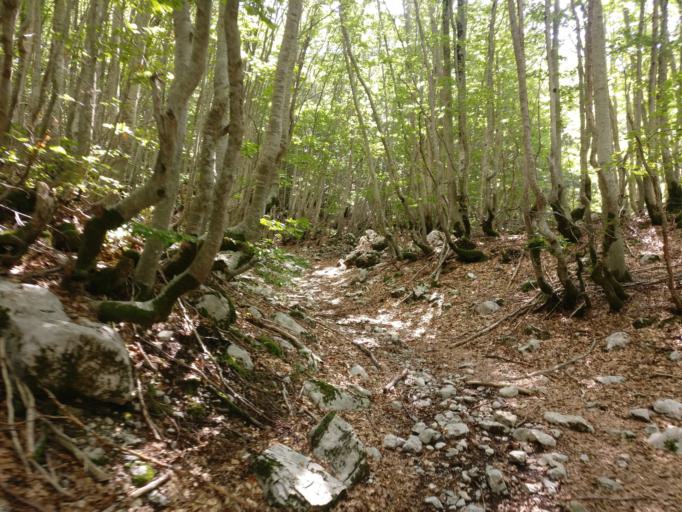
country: ME
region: Kotor
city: Kotor
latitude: 42.4097
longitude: 18.8398
